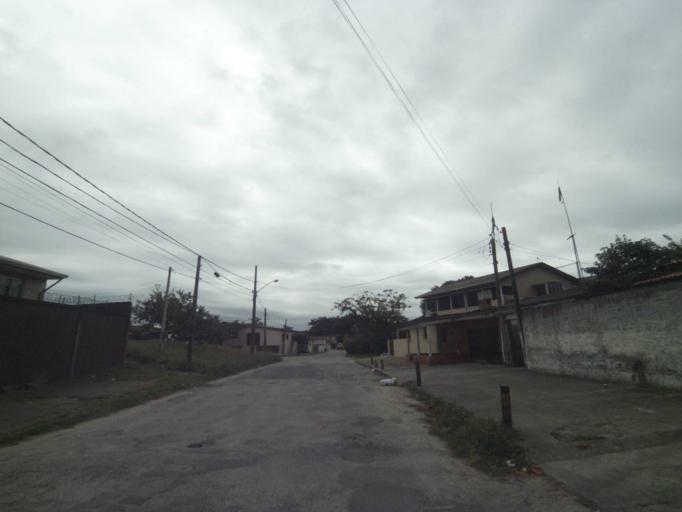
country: BR
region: Parana
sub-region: Paranagua
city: Paranagua
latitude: -25.5189
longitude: -48.5279
